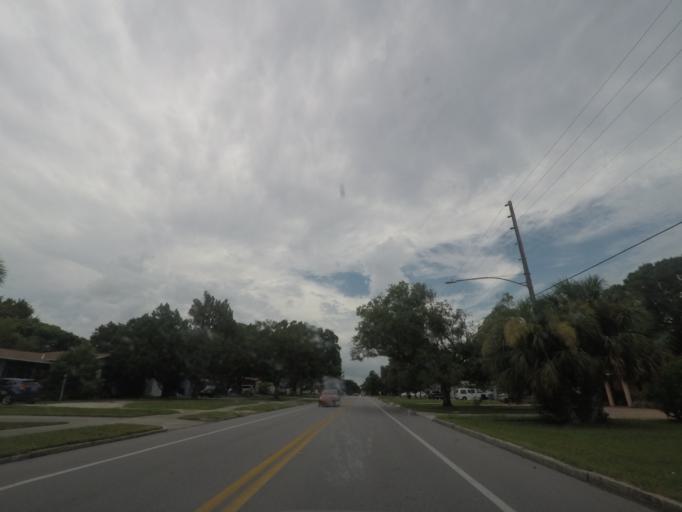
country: US
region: Florida
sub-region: Pinellas County
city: West and East Lealman
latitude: 27.7991
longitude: -82.6915
